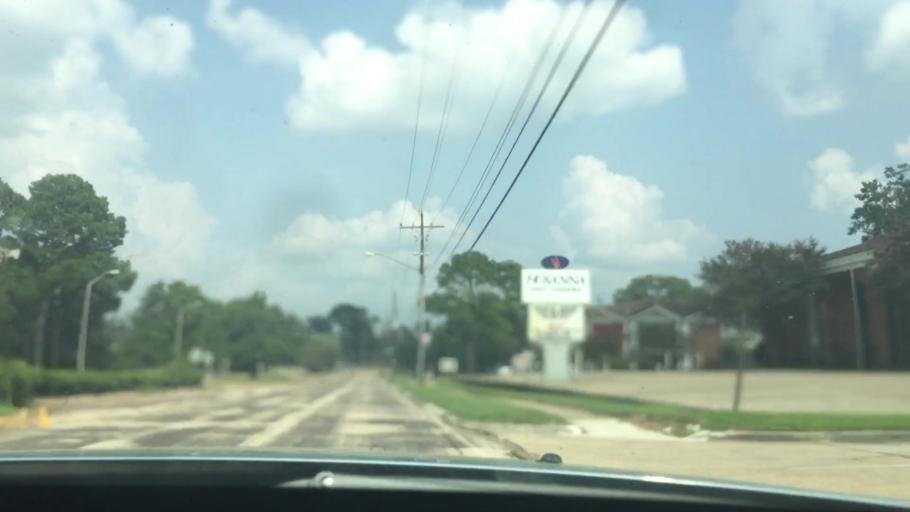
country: US
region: Louisiana
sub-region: East Baton Rouge Parish
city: Westminster
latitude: 30.4425
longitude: -91.0985
